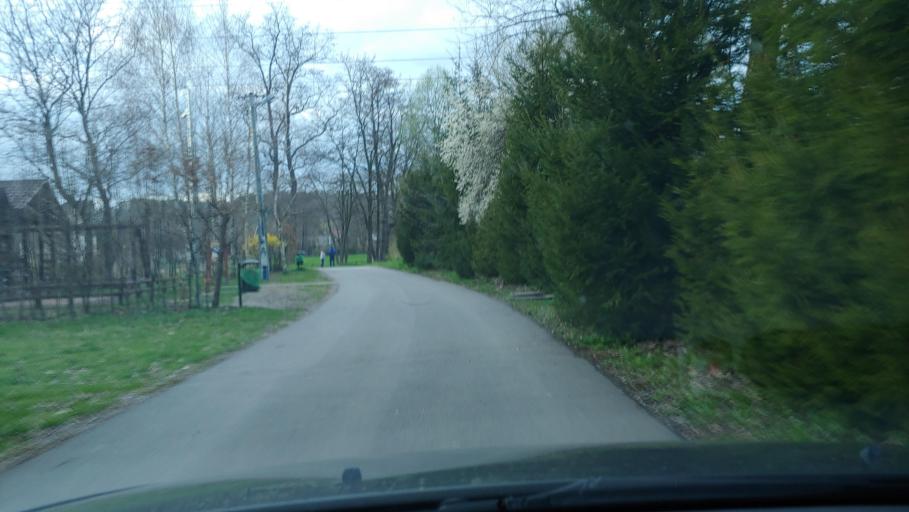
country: PL
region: Lesser Poland Voivodeship
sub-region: Powiat krakowski
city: Bolechowice
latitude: 50.1426
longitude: 19.7913
